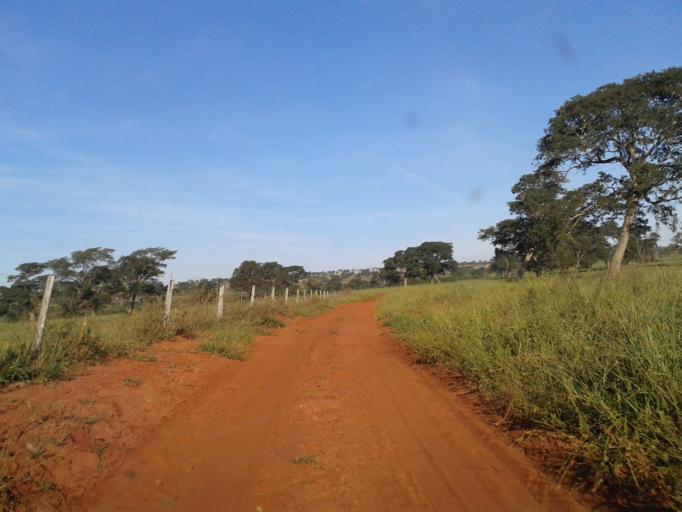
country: BR
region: Minas Gerais
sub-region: Santa Vitoria
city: Santa Vitoria
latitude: -19.0042
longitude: -50.3377
